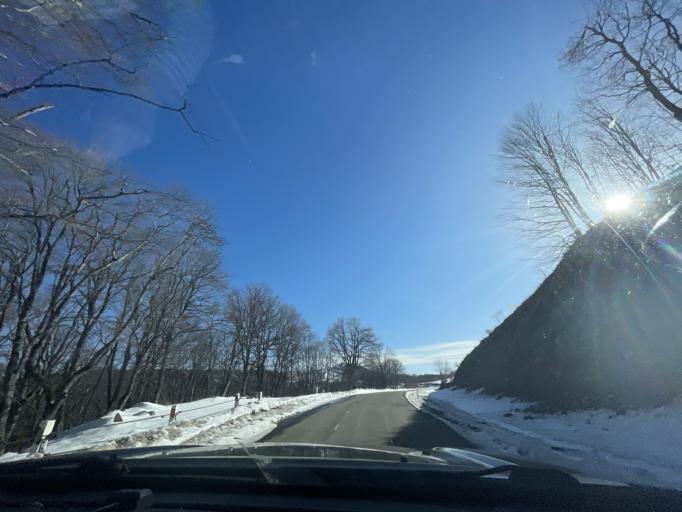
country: GE
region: Kvemo Kartli
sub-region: Tetri Tsqaro
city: Manglisi
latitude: 41.7678
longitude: 44.5074
